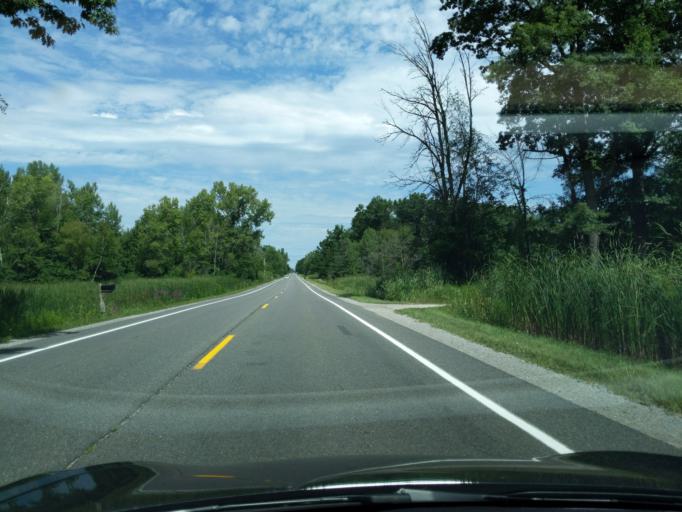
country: US
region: Michigan
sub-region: Midland County
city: Midland
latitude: 43.6008
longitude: -84.3693
